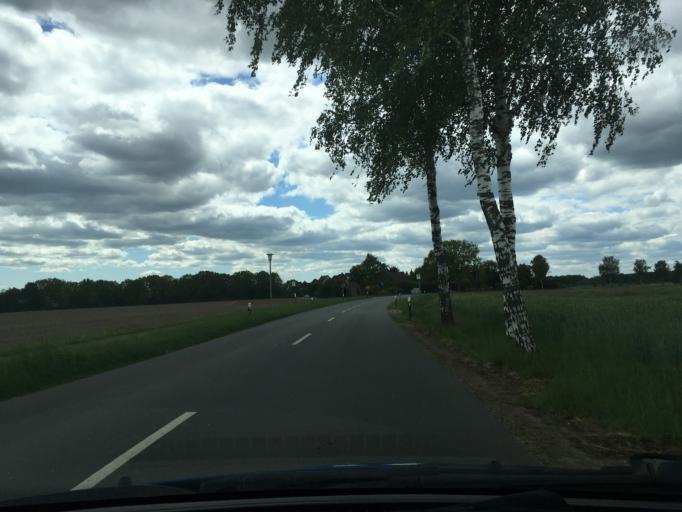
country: DE
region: Lower Saxony
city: Suderburg
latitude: 52.9325
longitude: 10.4816
